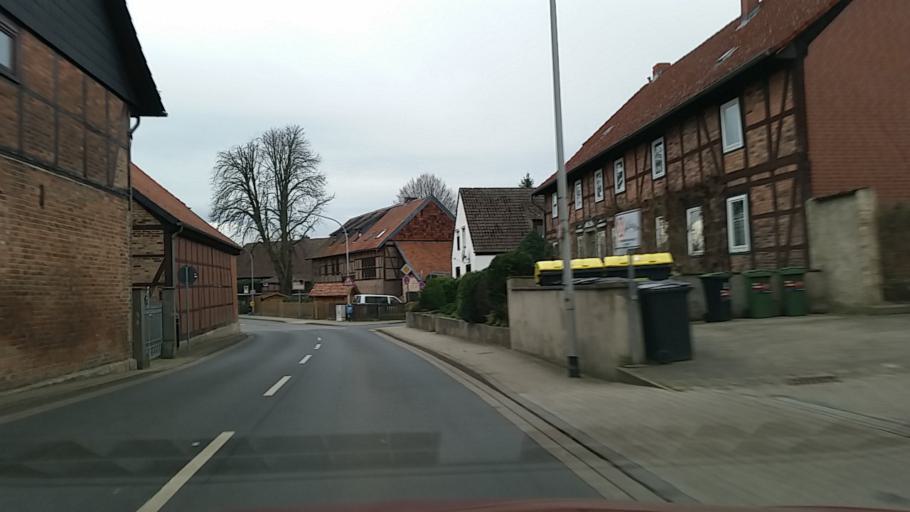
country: DE
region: Lower Saxony
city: Meine
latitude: 52.3421
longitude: 10.5779
